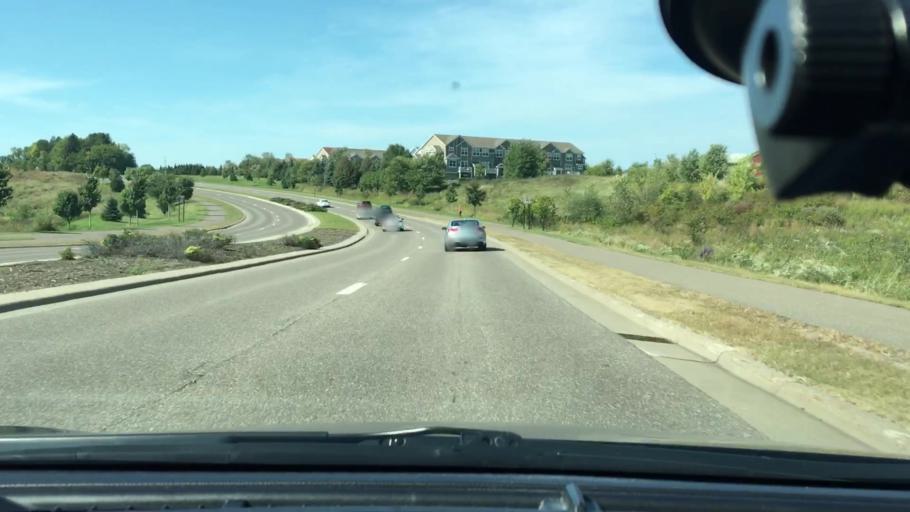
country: US
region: Minnesota
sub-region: Hennepin County
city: Maple Grove
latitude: 45.0845
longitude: -93.4924
